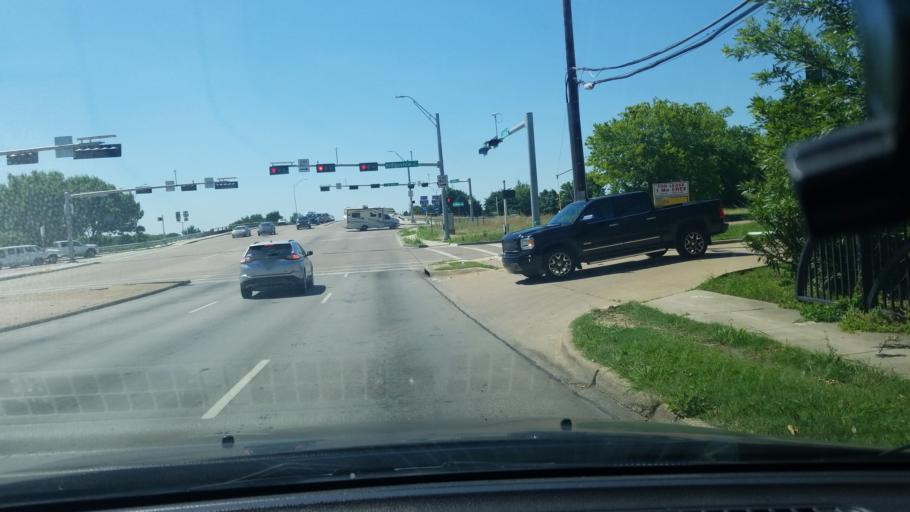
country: US
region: Texas
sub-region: Dallas County
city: Mesquite
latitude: 32.7801
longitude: -96.6229
